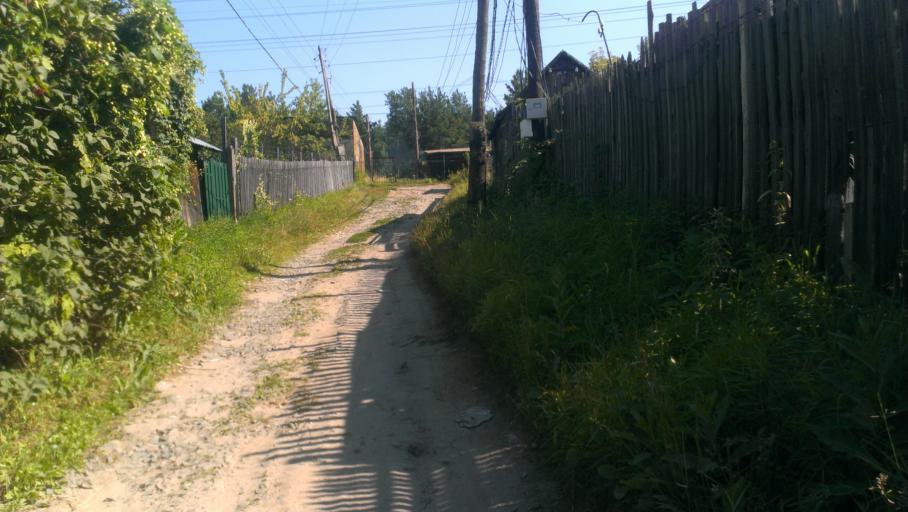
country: RU
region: Altai Krai
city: Novosilikatnyy
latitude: 53.3205
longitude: 83.6848
